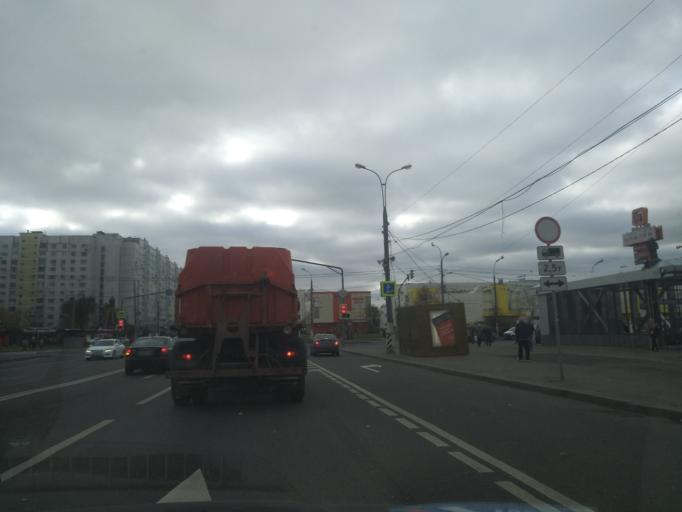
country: RU
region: Moscow
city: Otradnoye
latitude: 55.8645
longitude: 37.6059
